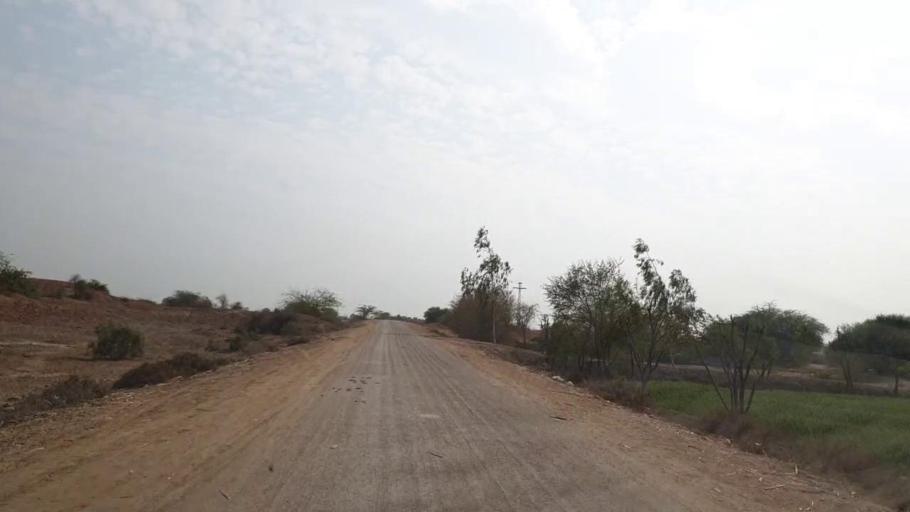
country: PK
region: Sindh
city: Mirpur Khas
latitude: 25.5545
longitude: 69.1701
